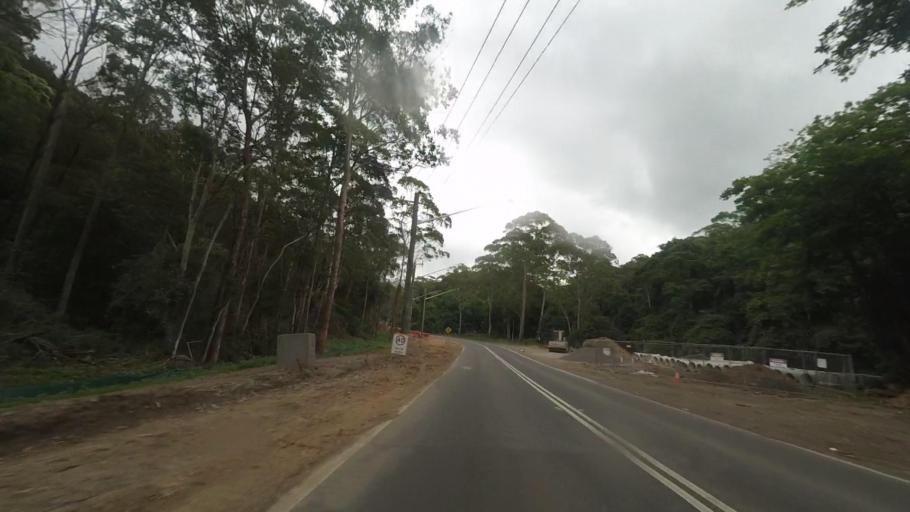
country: AU
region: New South Wales
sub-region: Wollongong
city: Cordeaux Heights
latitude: -34.4359
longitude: 150.8362
